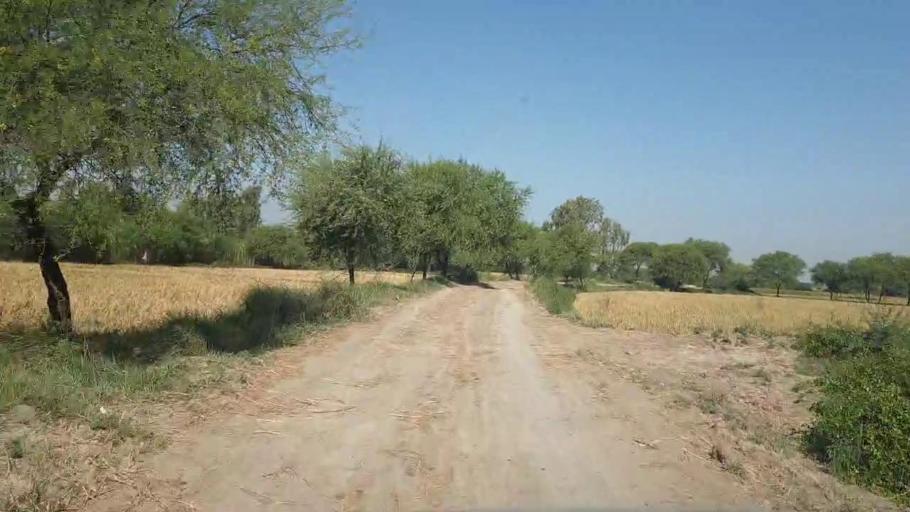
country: PK
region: Sindh
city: Talhar
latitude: 24.8090
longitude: 68.7863
